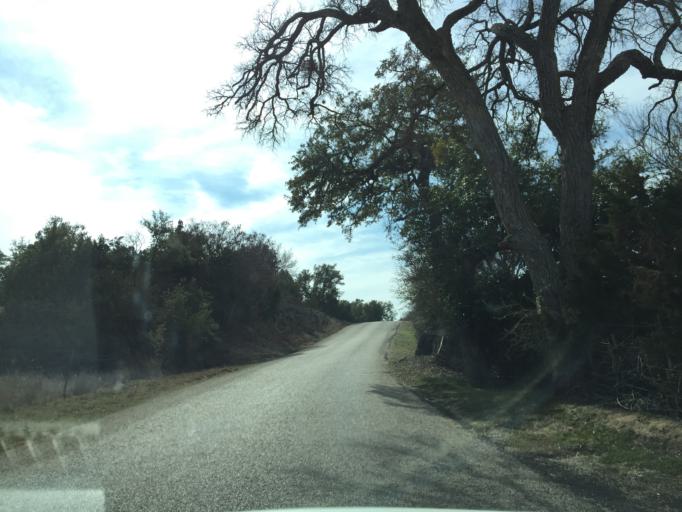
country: US
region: Texas
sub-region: Gillespie County
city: Fredericksburg
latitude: 30.3950
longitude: -98.7067
